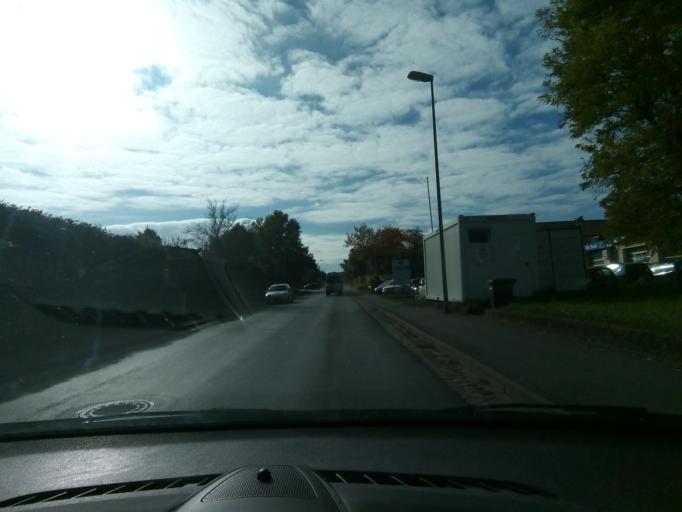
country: DE
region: Bavaria
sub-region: Regierungsbezirk Unterfranken
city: Gerolzhofen
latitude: 49.8964
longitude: 10.3524
